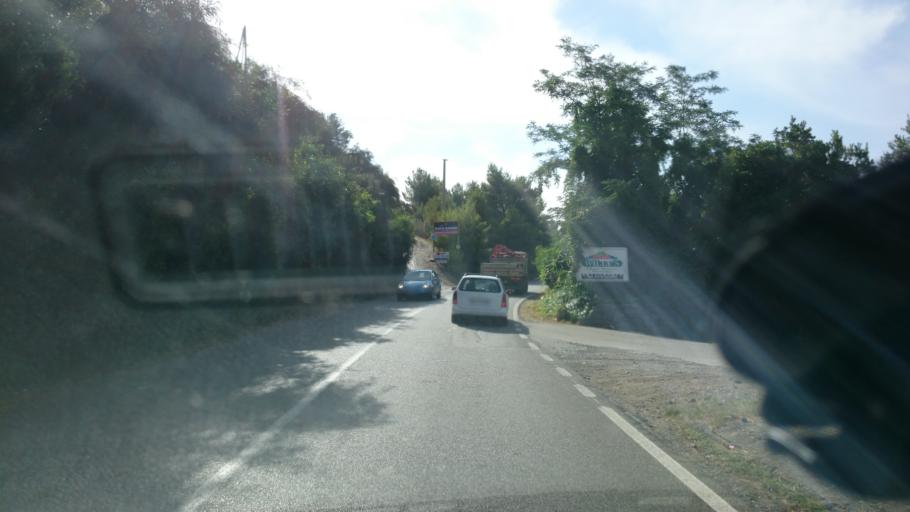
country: IT
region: Campania
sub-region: Provincia di Salerno
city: Marina di Camerota
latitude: 40.0080
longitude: 15.3525
